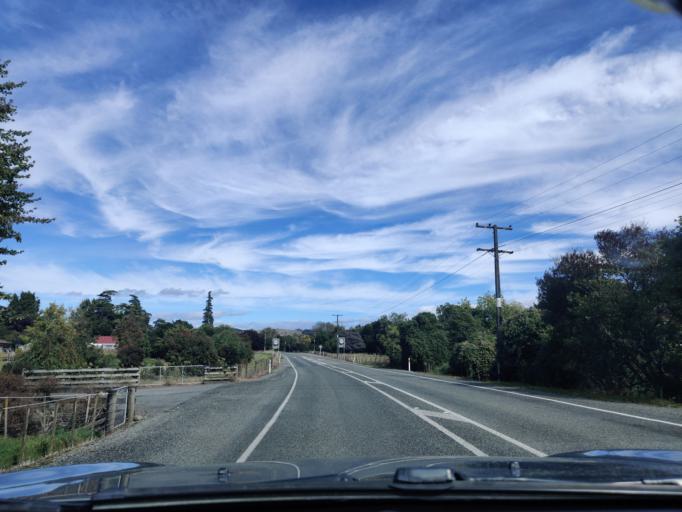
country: NZ
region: Tasman
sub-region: Tasman District
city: Wakefield
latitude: -41.4083
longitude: 173.0319
